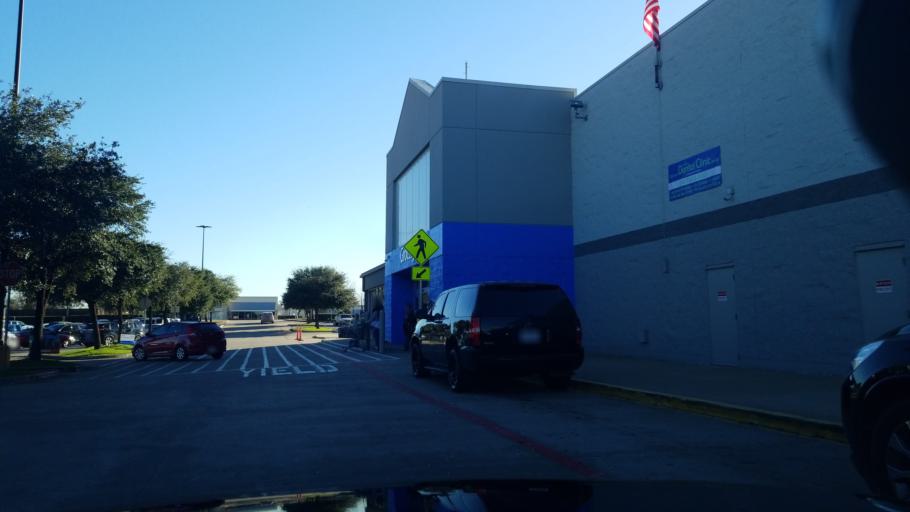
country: US
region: Texas
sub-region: Denton County
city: Hickory Creek
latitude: 33.1278
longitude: -97.0456
